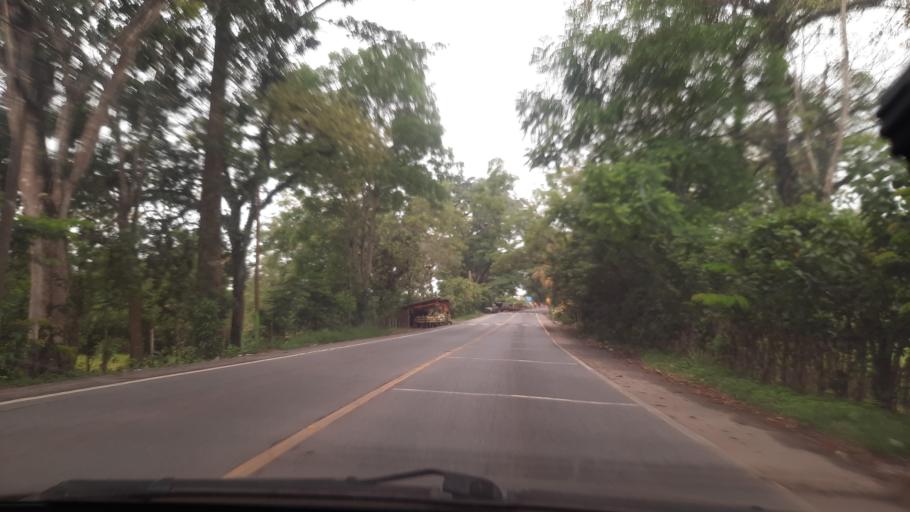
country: GT
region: Izabal
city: Morales
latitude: 15.5065
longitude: -88.8096
